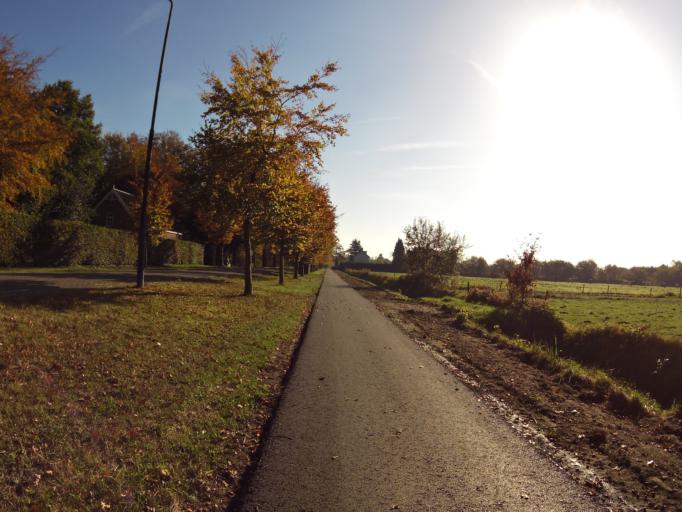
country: NL
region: North Brabant
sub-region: Gemeente Vught
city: Vught
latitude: 51.6308
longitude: 5.2810
